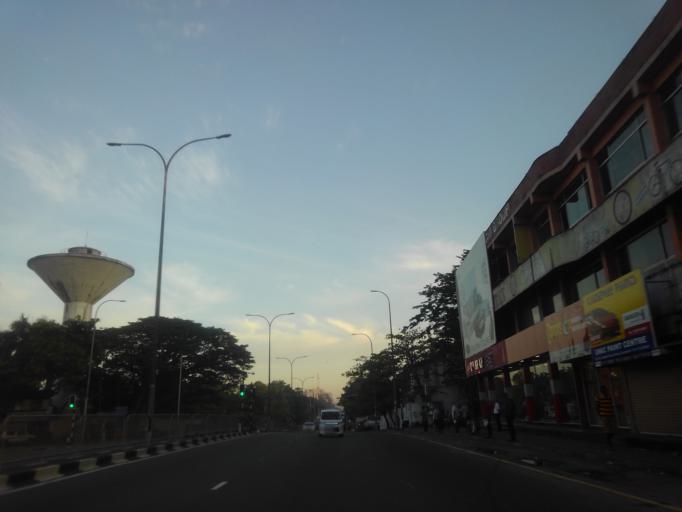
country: LK
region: Western
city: Kolonnawa
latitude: 6.9164
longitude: 79.8777
